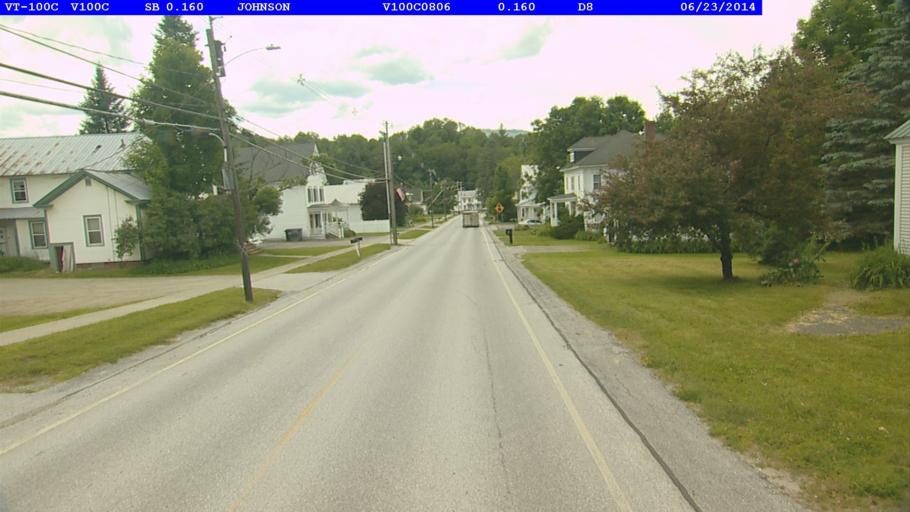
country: US
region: Vermont
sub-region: Lamoille County
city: Johnson
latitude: 44.6345
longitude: -72.6733
